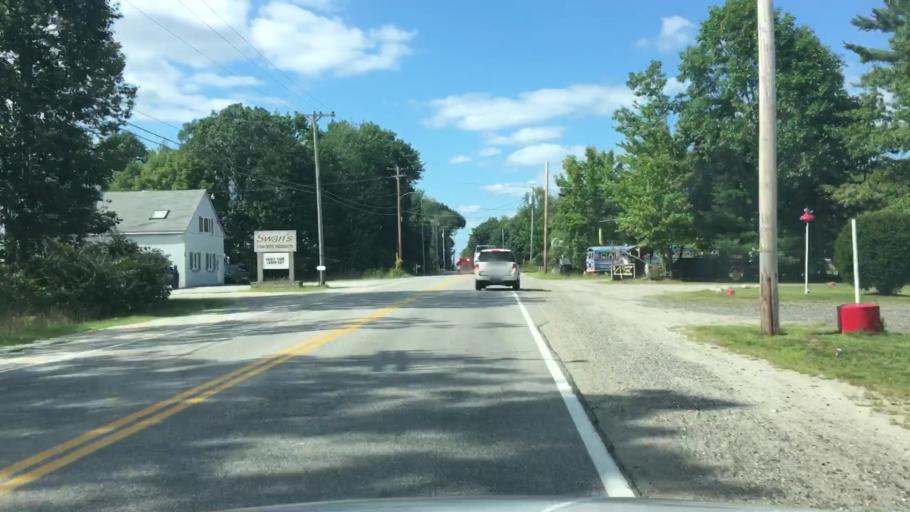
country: US
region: Maine
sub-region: Cumberland County
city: Westbrook
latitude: 43.7238
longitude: -70.3406
